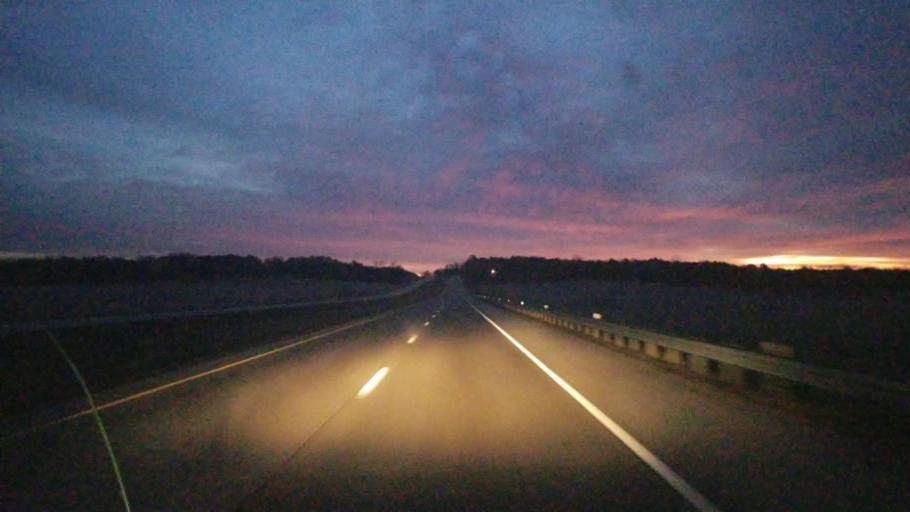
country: US
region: Missouri
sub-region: Howell County
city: Mountain View
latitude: 36.9896
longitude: -91.5313
